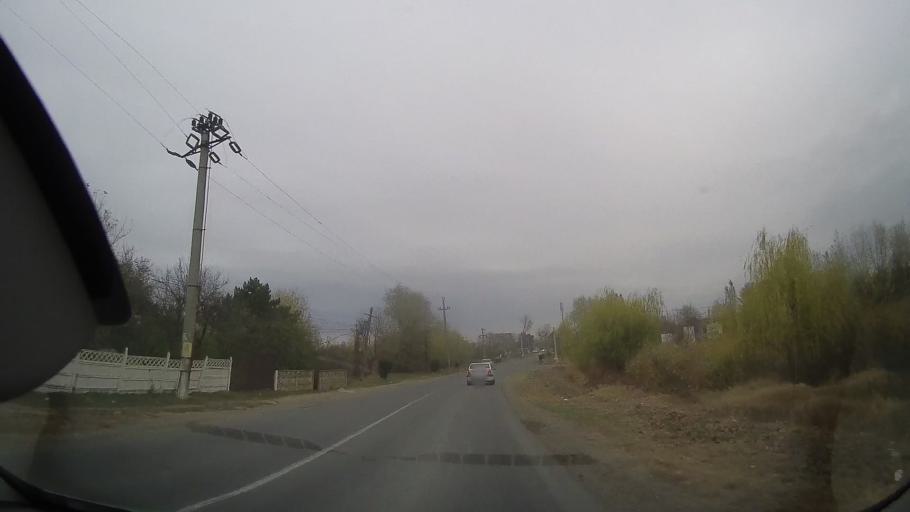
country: RO
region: Ialomita
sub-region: Oras Amara
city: Amara
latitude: 44.6114
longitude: 27.3146
